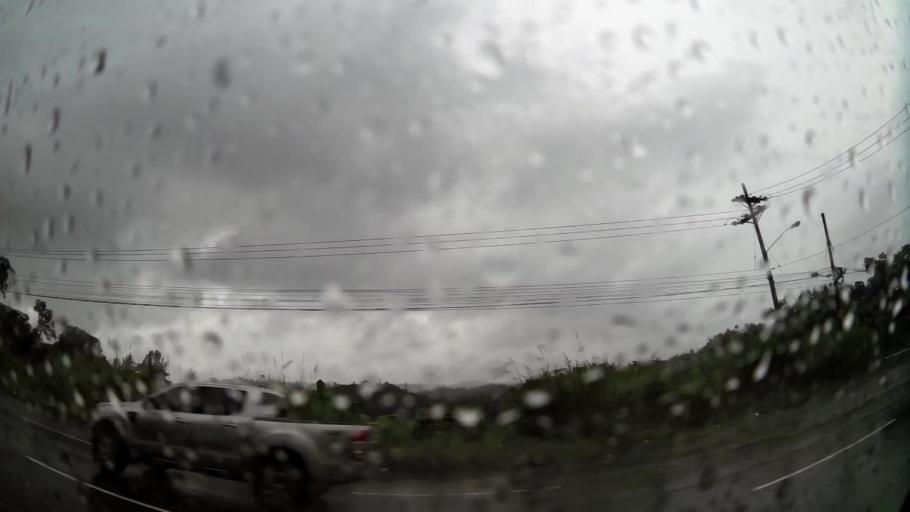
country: PA
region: Colon
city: Quebrada Bonita Adentro
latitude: 9.2834
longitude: -79.7113
